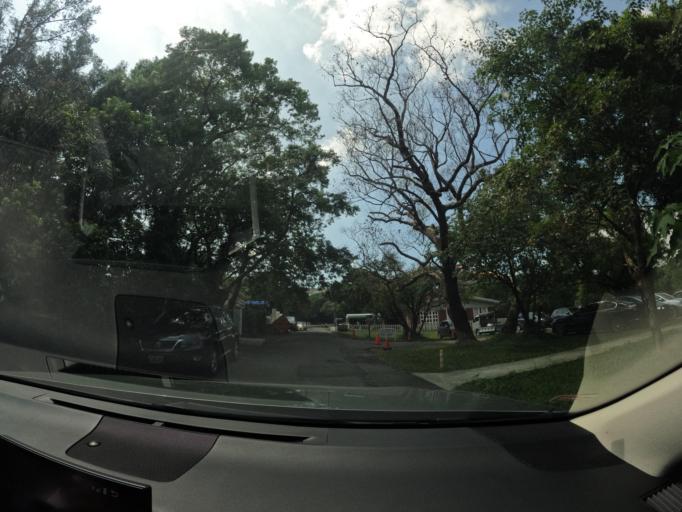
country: TW
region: Taipei
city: Taipei
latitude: 25.1359
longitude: 121.5416
